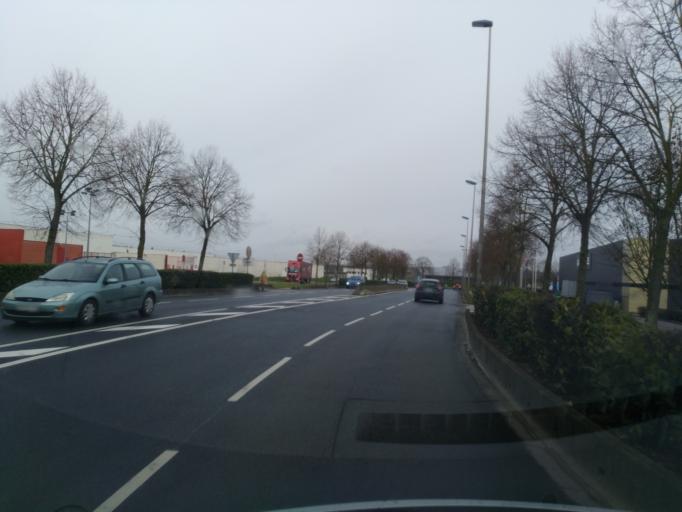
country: FR
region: Ile-de-France
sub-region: Departement des Yvelines
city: Plaisir
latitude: 48.8281
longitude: 1.9639
